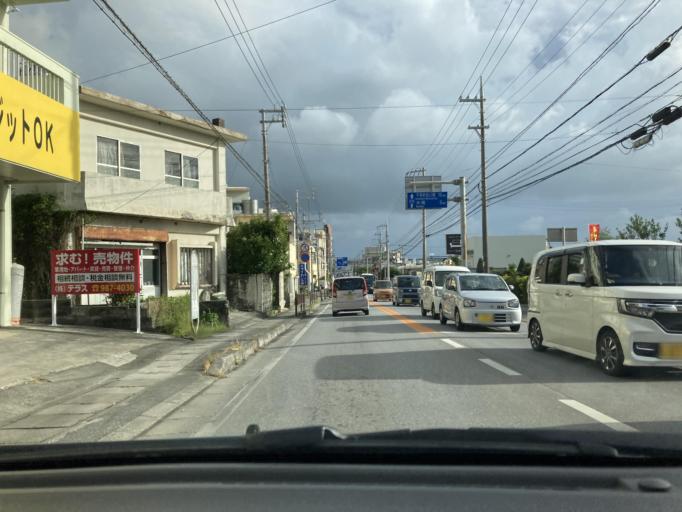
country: JP
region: Okinawa
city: Tomigusuku
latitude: 26.1791
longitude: 127.6648
